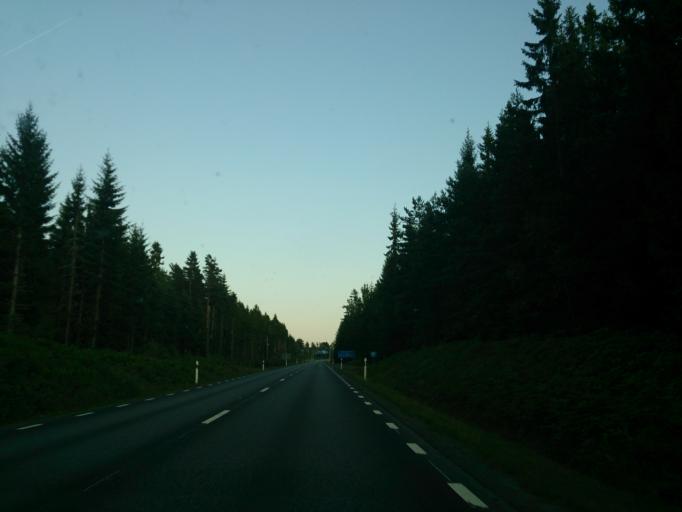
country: SE
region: Joenkoeping
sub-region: Varnamo Kommun
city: Rydaholm
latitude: 57.0361
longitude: 14.2456
